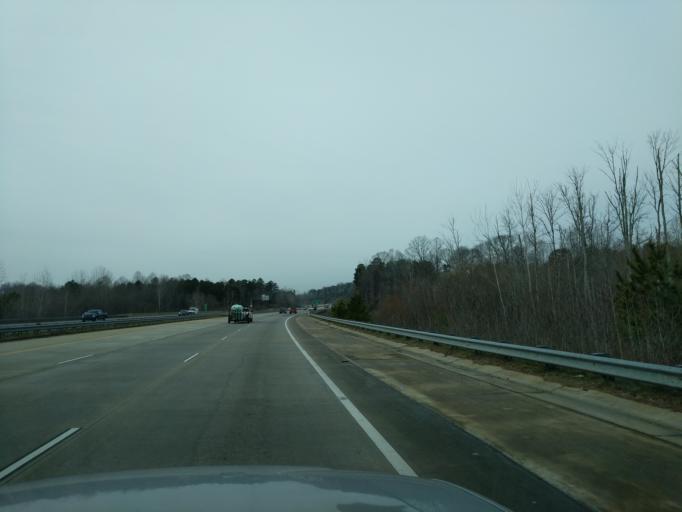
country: US
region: North Carolina
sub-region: Mecklenburg County
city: Huntersville
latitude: 35.3397
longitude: -80.8918
